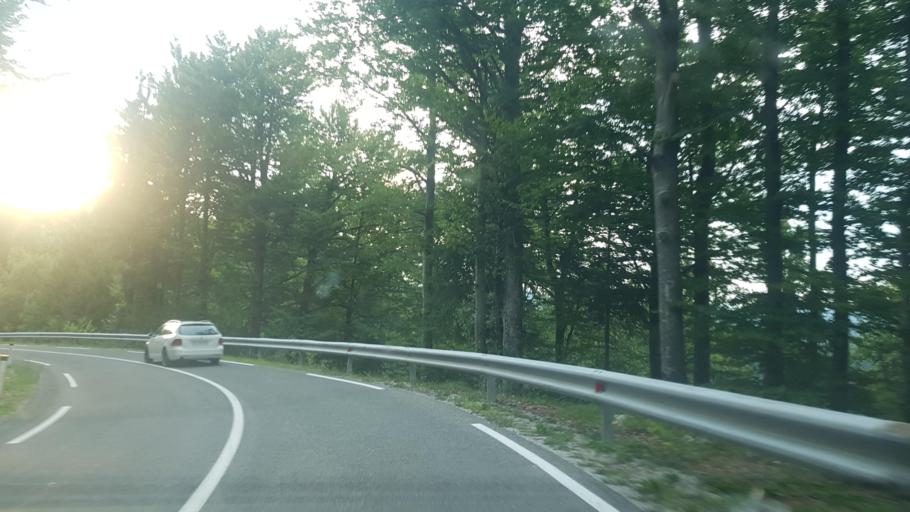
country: SI
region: Logatec
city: Logatec
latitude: 45.8906
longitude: 14.1561
